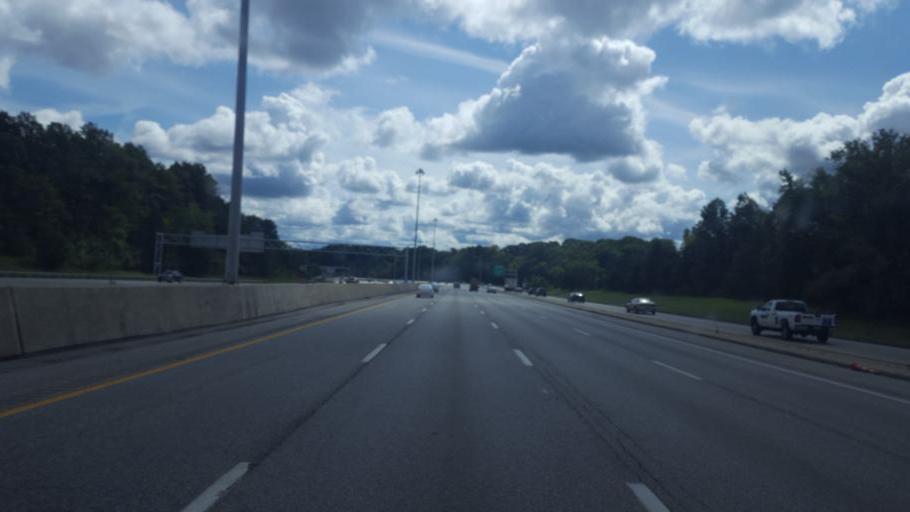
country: US
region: Ohio
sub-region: Cuyahoga County
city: Brooklyn Heights
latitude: 41.4150
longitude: -81.6749
